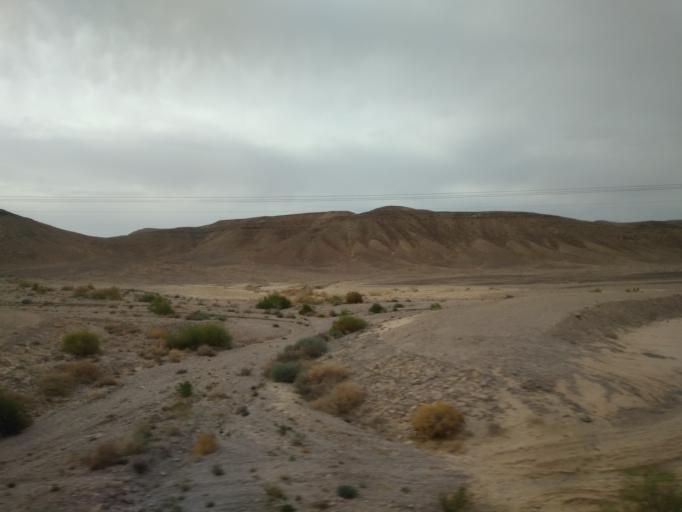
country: IL
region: Southern District
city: Eilat
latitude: 29.9555
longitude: 34.9228
